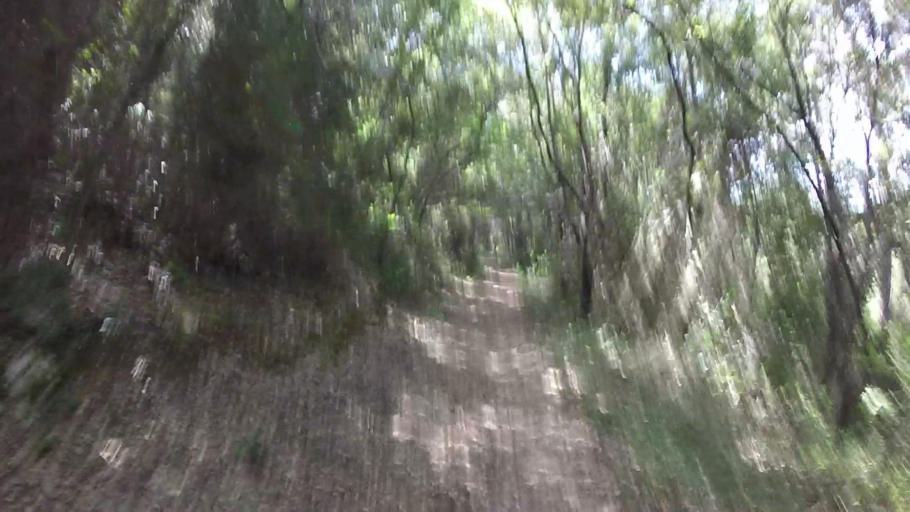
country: FR
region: Provence-Alpes-Cote d'Azur
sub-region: Departement des Alpes-Maritimes
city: Mougins
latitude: 43.6164
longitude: 7.0283
